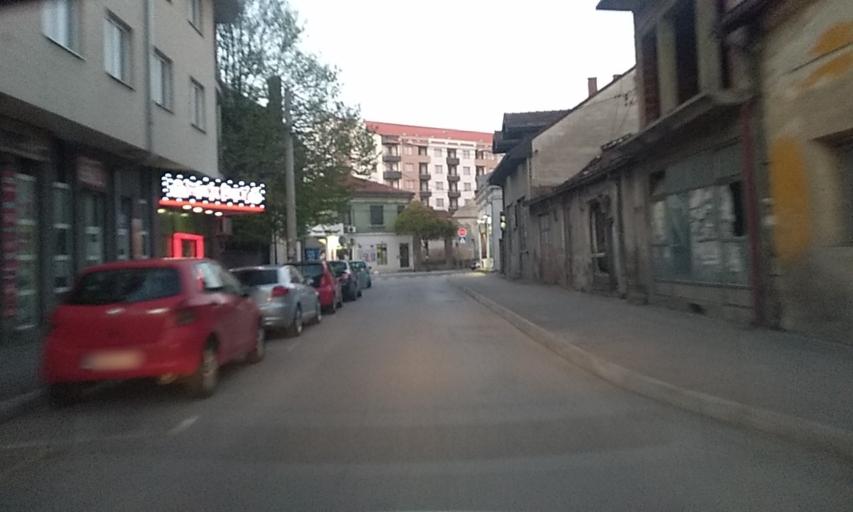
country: RS
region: Central Serbia
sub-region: Nisavski Okrug
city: Nis
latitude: 43.3165
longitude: 21.8895
